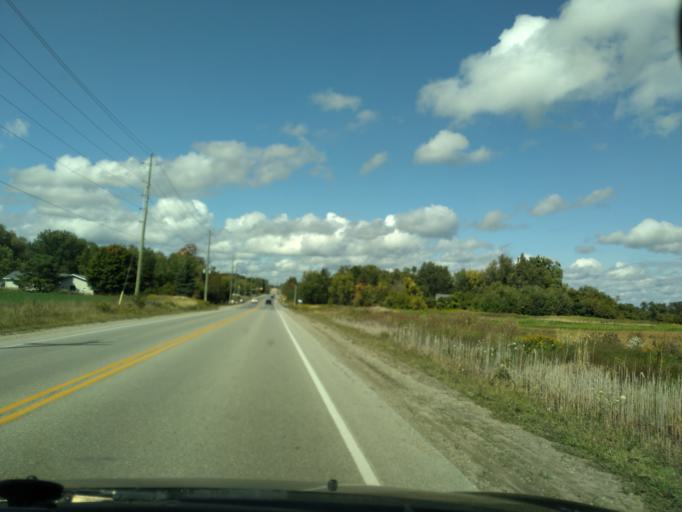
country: CA
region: Ontario
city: Innisfil
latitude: 44.2929
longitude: -79.5726
